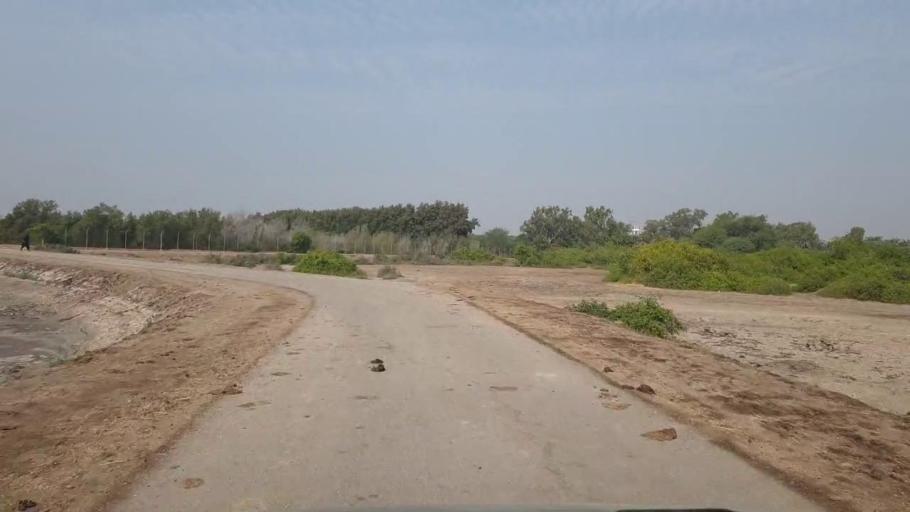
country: PK
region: Sindh
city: Tando Muhammad Khan
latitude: 25.1281
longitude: 68.4552
